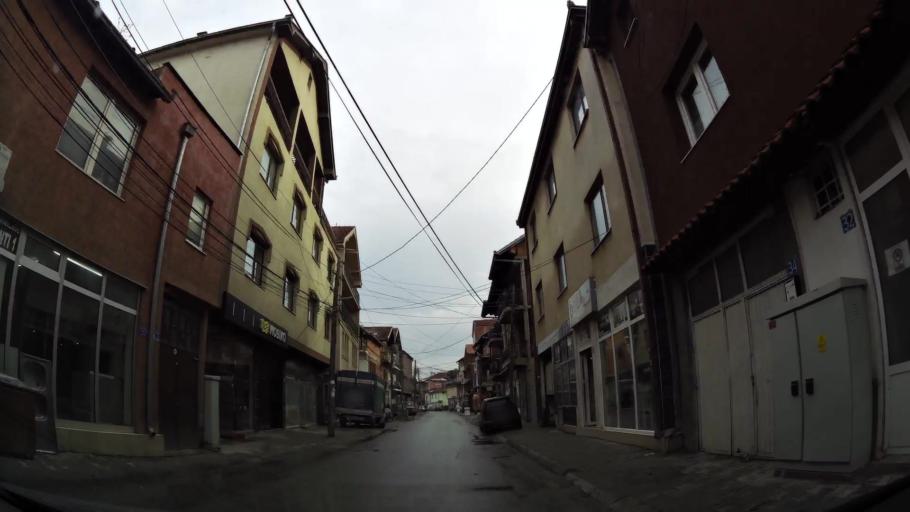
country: XK
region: Pristina
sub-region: Komuna e Prishtines
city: Pristina
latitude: 42.6726
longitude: 21.1666
